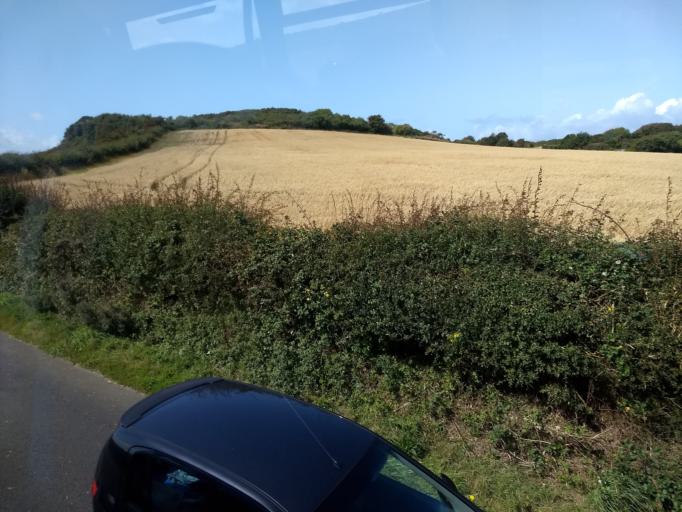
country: GB
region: England
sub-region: Isle of Wight
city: Totland
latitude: 50.6729
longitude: -1.5495
